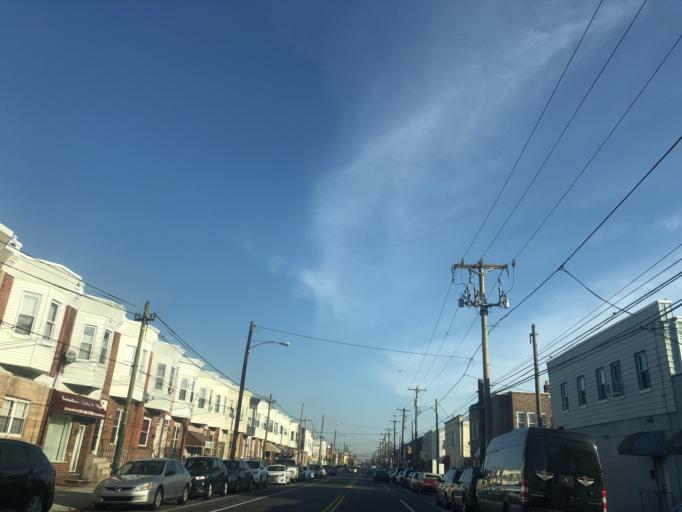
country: US
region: Pennsylvania
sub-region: Philadelphia County
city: Philadelphia
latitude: 39.9258
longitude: -75.1809
